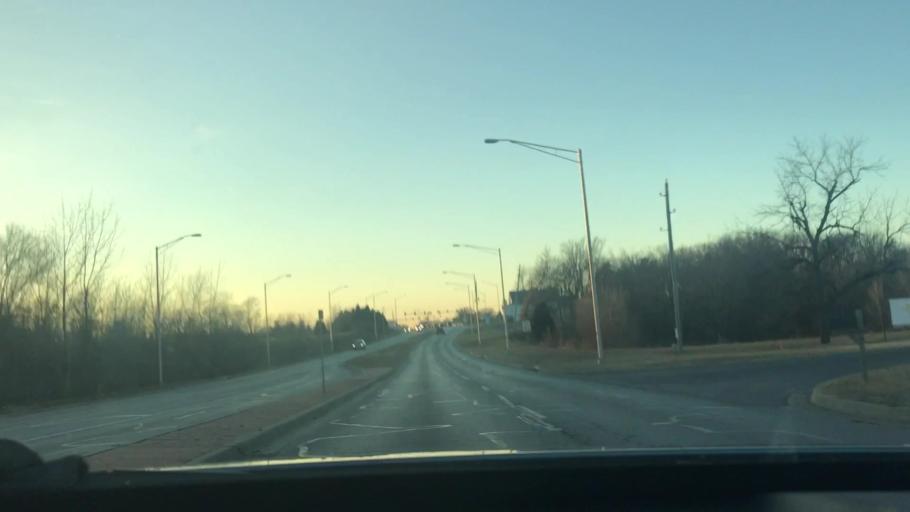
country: US
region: Missouri
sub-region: Jackson County
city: Lees Summit
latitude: 38.9823
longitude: -94.3515
